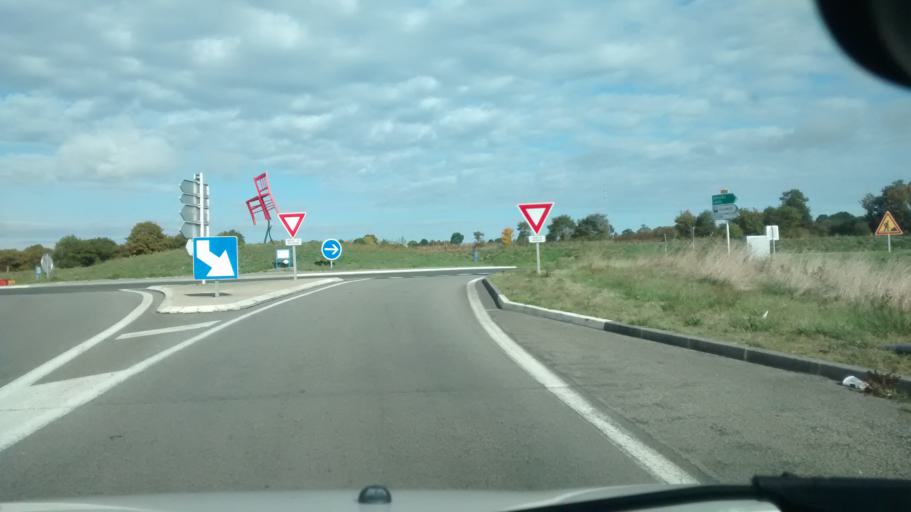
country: FR
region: Pays de la Loire
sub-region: Departement de Maine-et-Loire
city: Pouance
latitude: 47.7603
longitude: -1.2042
